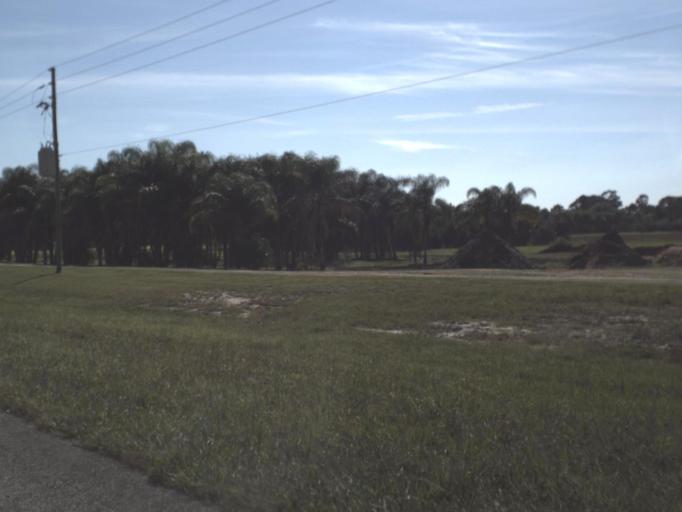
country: US
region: Florida
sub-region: Highlands County
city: Lake Placid
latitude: 27.3458
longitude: -81.3872
